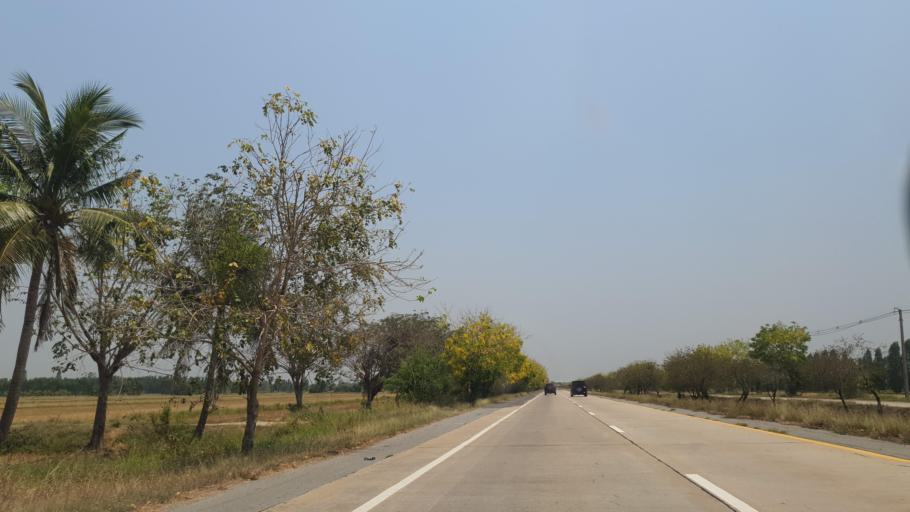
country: TH
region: Suphan Buri
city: Suphan Buri
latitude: 14.5095
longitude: 100.0511
